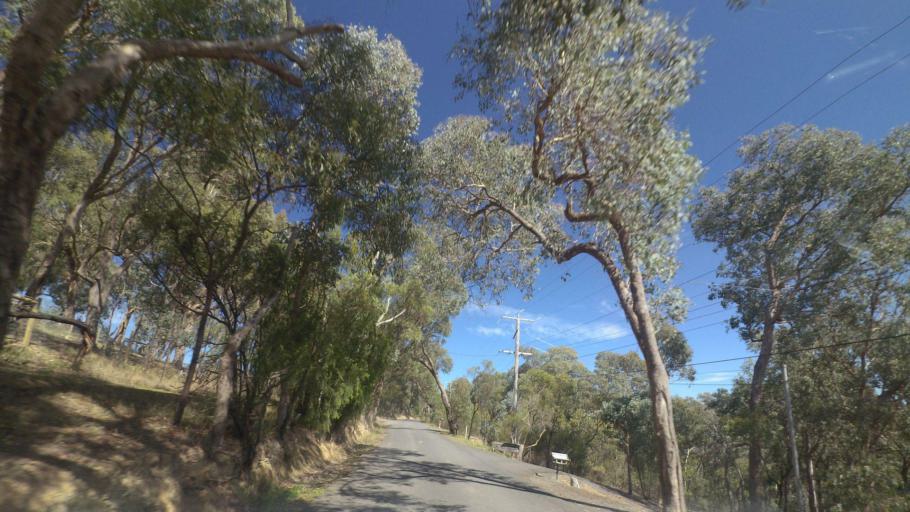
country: AU
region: Victoria
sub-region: Manningham
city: Warrandyte
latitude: -37.7439
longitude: 145.2252
